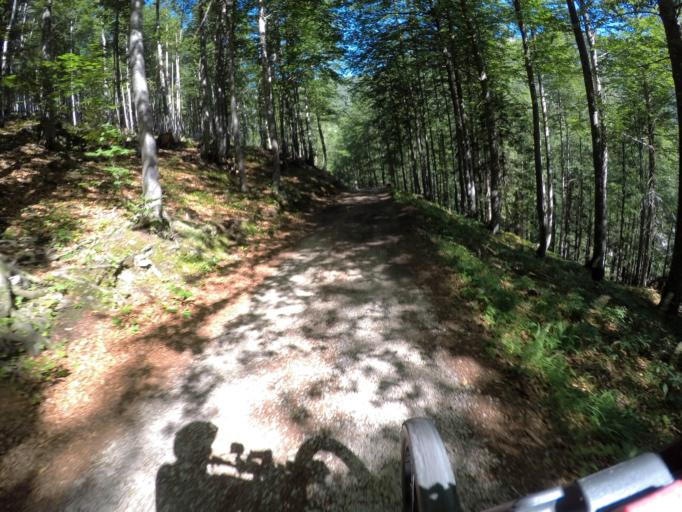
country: IT
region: Friuli Venezia Giulia
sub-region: Provincia di Udine
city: Malborghetto
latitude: 46.4592
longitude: 13.4528
